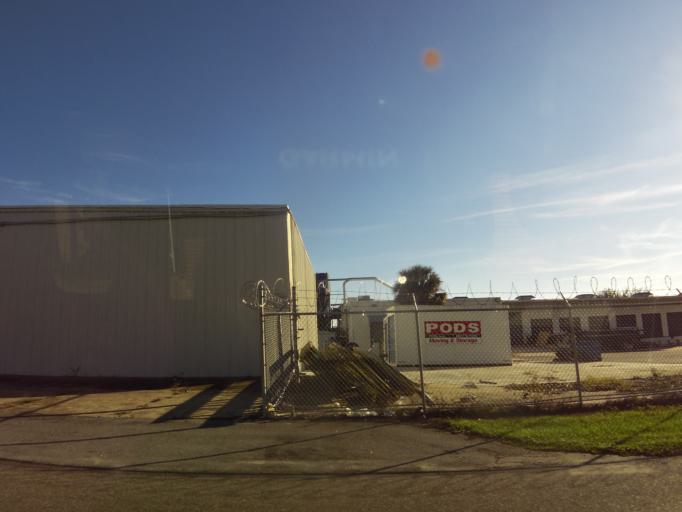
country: US
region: Florida
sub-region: Duval County
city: Jacksonville
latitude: 30.3394
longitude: -81.6777
